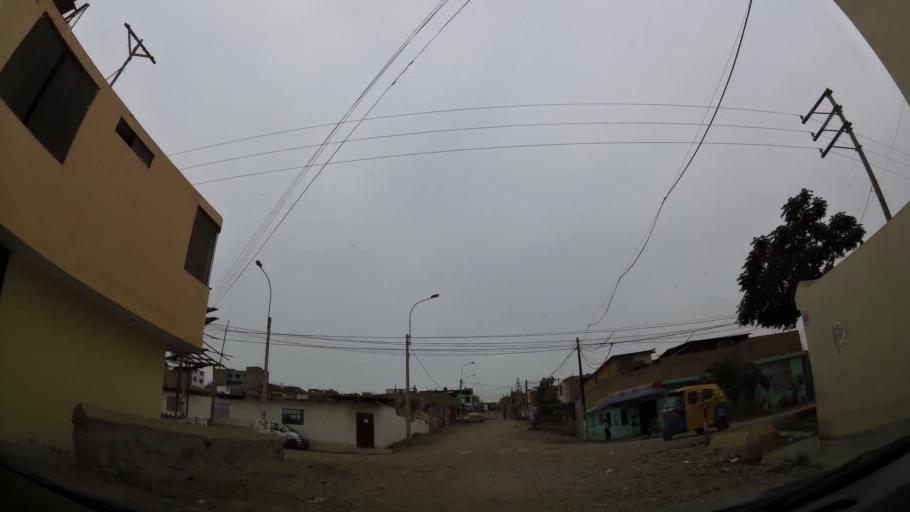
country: PE
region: Lima
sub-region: Lima
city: Surco
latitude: -12.2009
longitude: -76.9849
